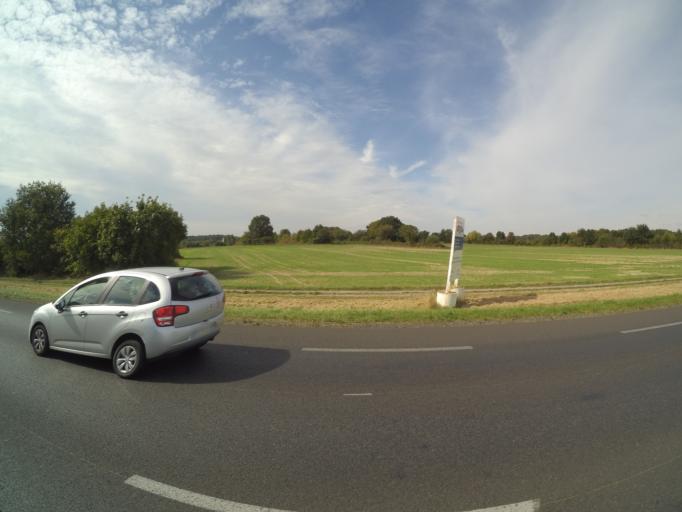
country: FR
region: Pays de la Loire
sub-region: Departement de Maine-et-Loire
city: Distre
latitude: 47.2382
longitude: -0.1119
